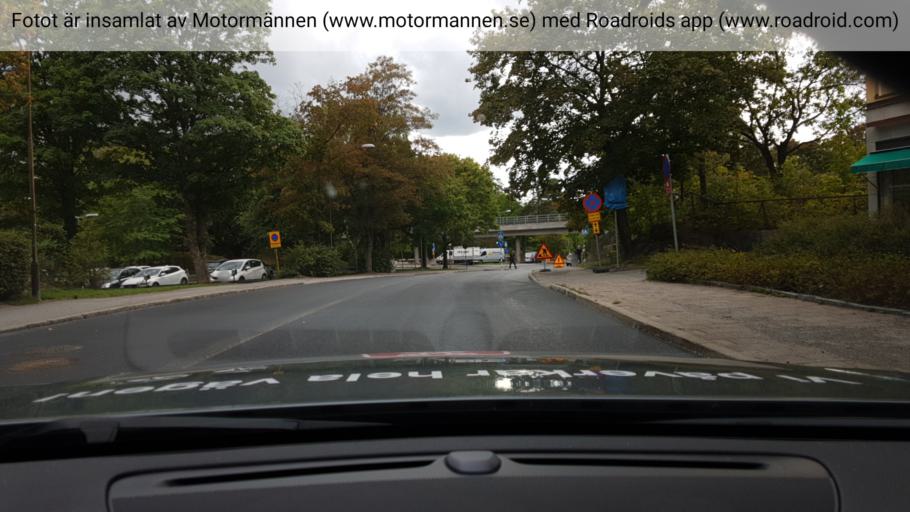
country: SE
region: Stockholm
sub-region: Huddinge Kommun
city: Huddinge
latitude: 59.2615
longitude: 18.0162
